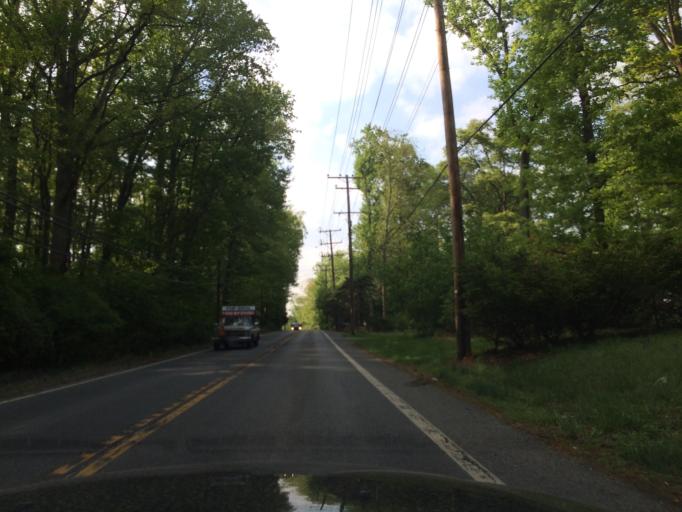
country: US
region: Maryland
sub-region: Howard County
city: Highland
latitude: 39.1760
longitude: -76.9550
